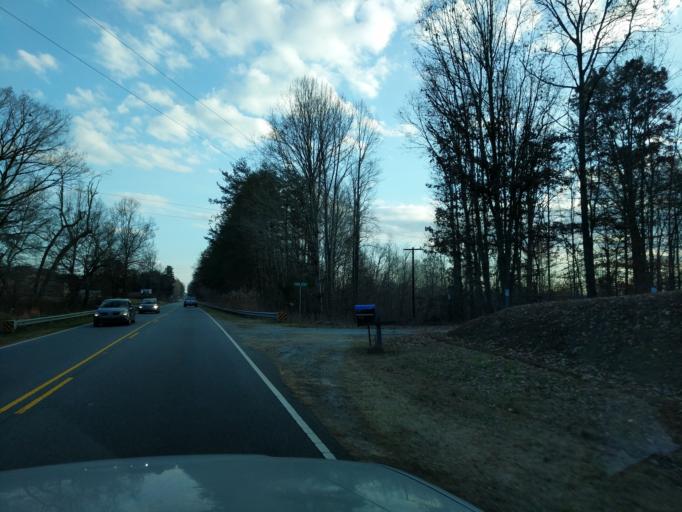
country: US
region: North Carolina
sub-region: Rutherford County
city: Rutherfordton
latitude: 35.4251
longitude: -81.9795
